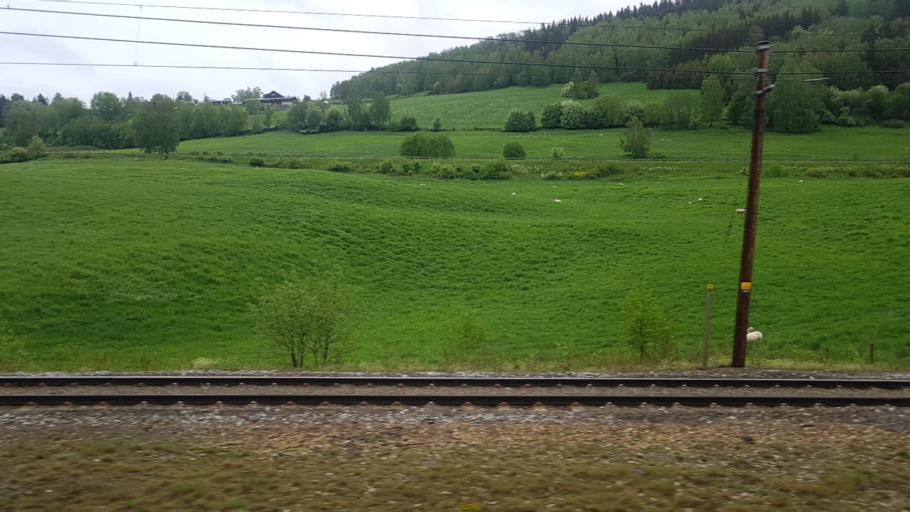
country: NO
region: Oppland
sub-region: Sor-Fron
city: Hundorp
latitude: 61.5475
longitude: 9.9605
